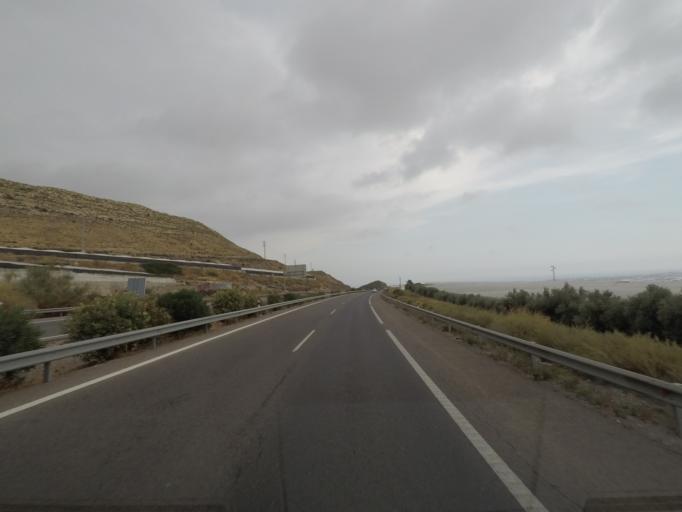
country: ES
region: Andalusia
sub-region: Provincia de Almeria
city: Vicar
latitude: 36.8131
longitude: -2.6421
